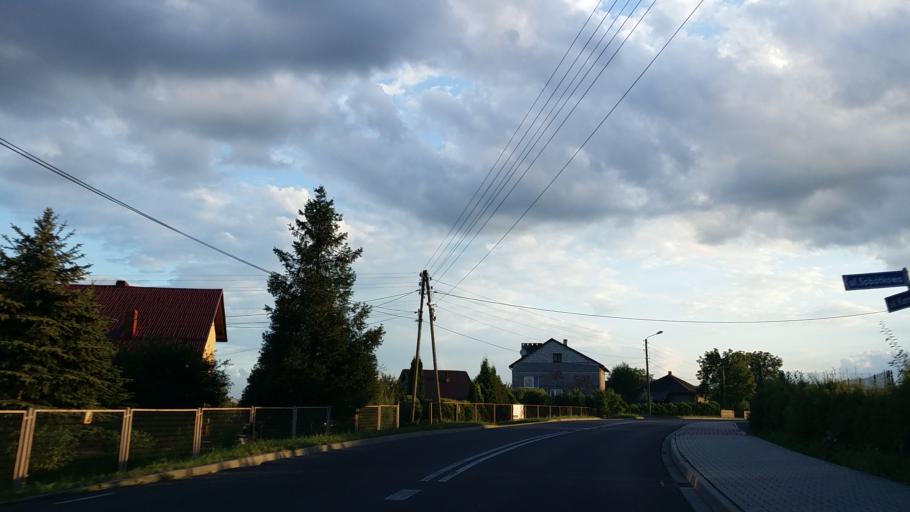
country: PL
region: Lesser Poland Voivodeship
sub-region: Powiat oswiecimski
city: Osiek
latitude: 49.9470
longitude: 19.2604
